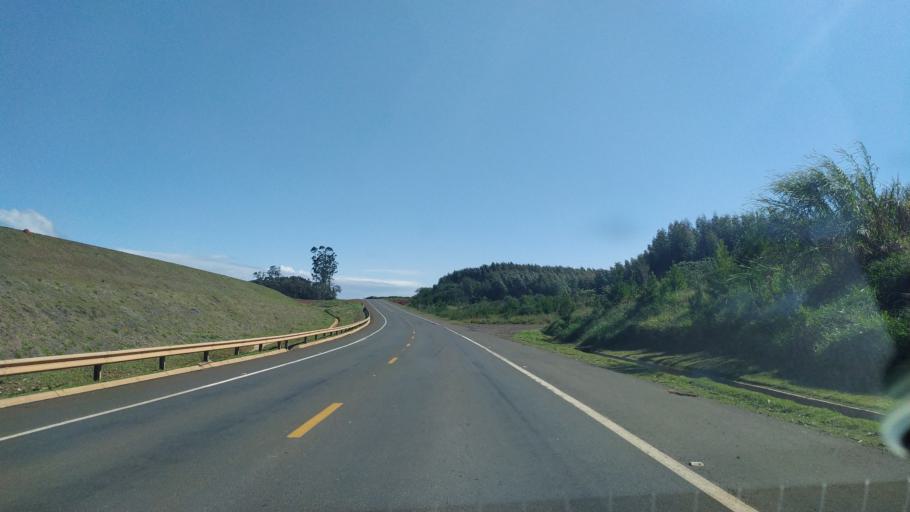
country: BR
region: Parana
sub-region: Ortigueira
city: Ortigueira
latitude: -24.2559
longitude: -50.7983
